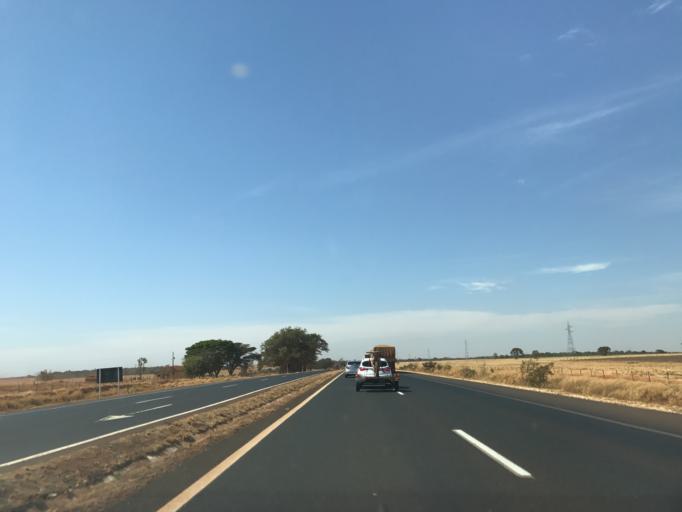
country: BR
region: Minas Gerais
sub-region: Centralina
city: Centralina
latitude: -18.6820
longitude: -49.1548
